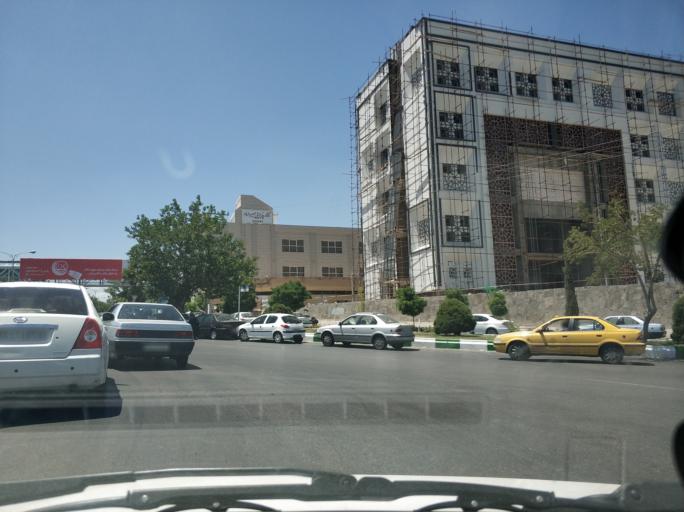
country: IR
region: Razavi Khorasan
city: Mashhad
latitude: 36.3145
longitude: 59.4899
